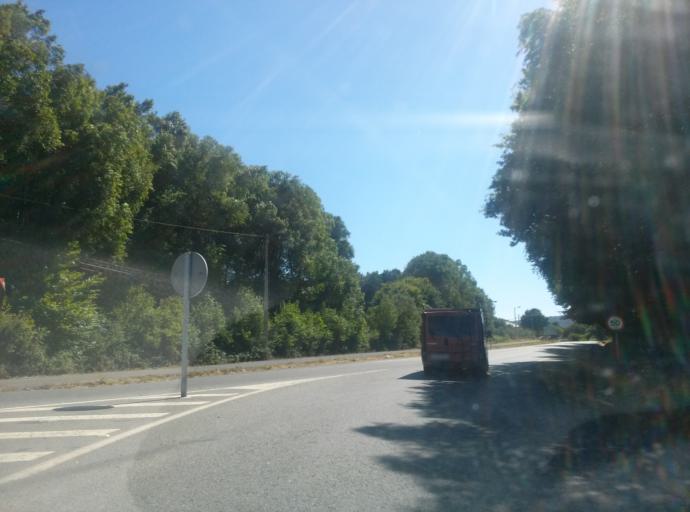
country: ES
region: Galicia
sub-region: Provincia de Lugo
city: Outeiro de Rei
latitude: 43.1052
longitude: -7.6074
